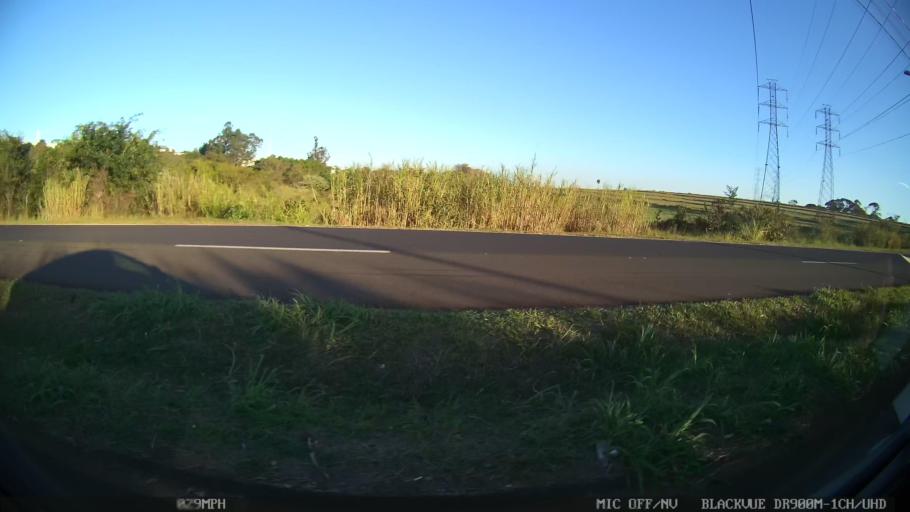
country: BR
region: Sao Paulo
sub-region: Araraquara
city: Araraquara
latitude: -21.7881
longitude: -48.2135
